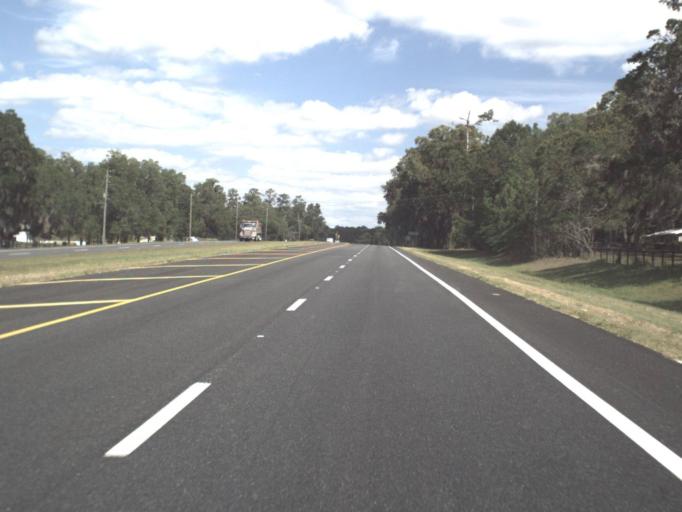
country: US
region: Florida
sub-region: Marion County
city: Ocala
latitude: 29.2517
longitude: -82.3019
